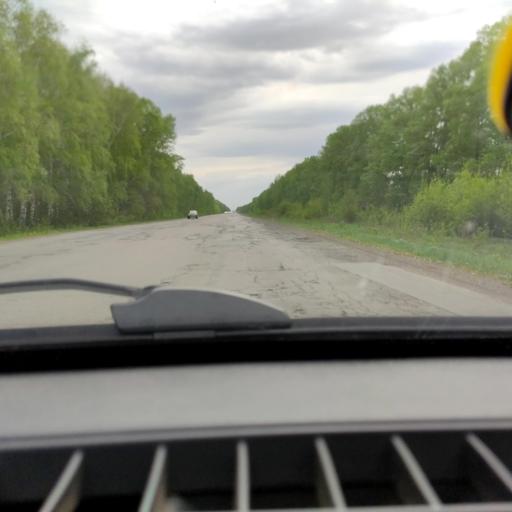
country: RU
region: Samara
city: Tol'yatti
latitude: 53.6488
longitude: 49.4224
